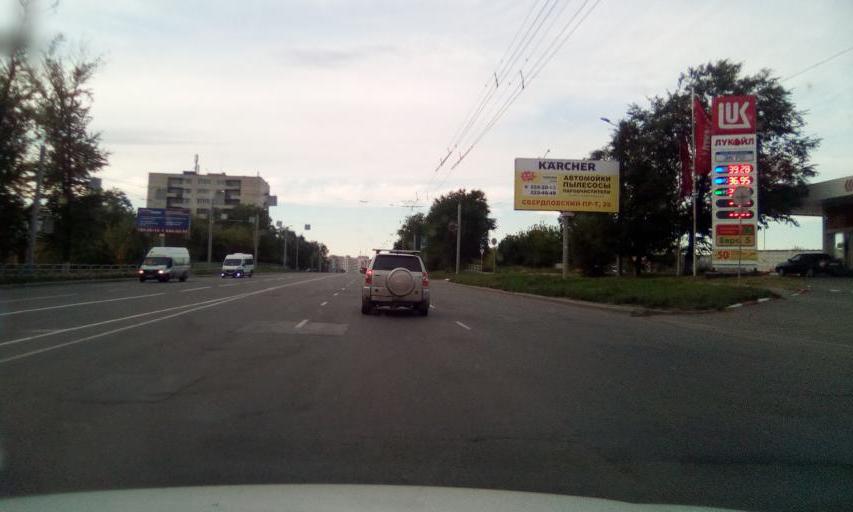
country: RU
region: Chelyabinsk
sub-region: Gorod Chelyabinsk
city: Chelyabinsk
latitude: 55.1615
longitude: 61.4516
